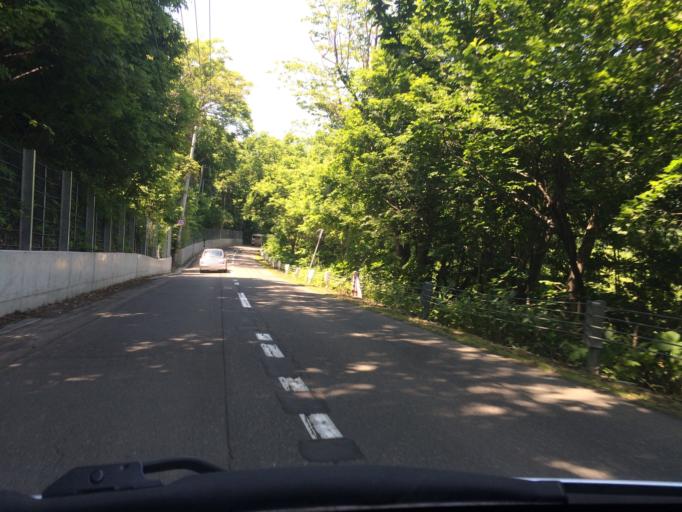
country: JP
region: Hokkaido
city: Sapporo
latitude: 42.9639
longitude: 141.2799
